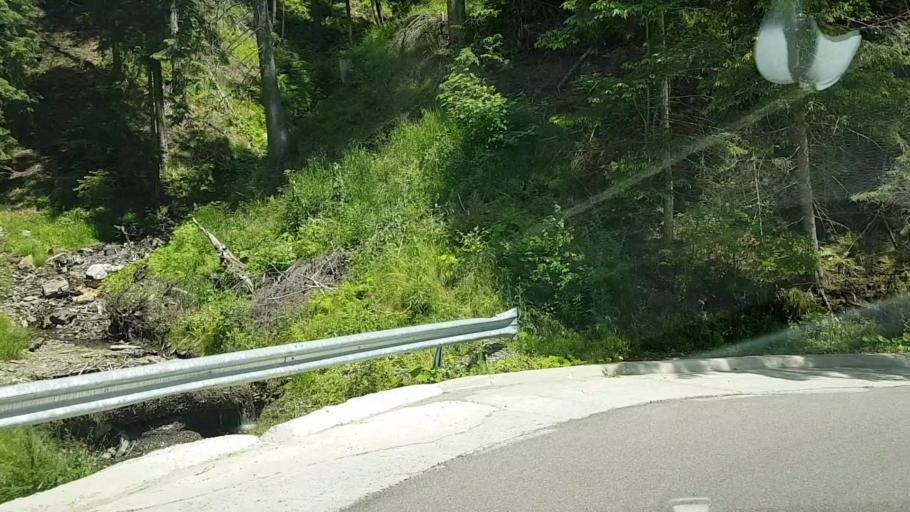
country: RO
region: Suceava
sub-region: Municipiul Campulung Moldovenesc
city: Campulung Moldovenesc
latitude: 47.4390
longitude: 25.5585
